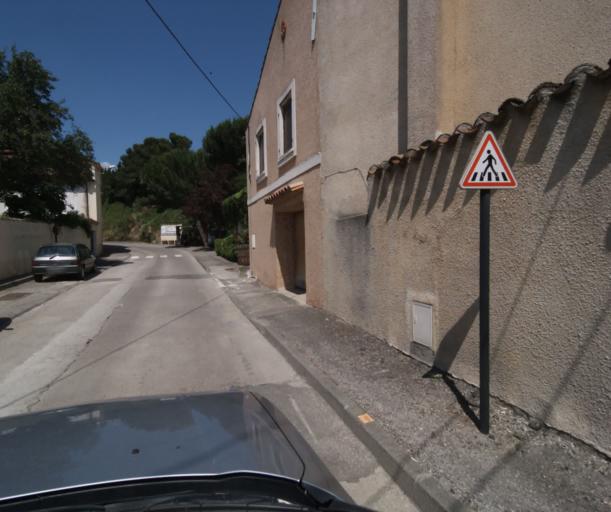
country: FR
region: Languedoc-Roussillon
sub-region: Departement de l'Aude
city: Limoux
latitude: 43.0521
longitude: 2.2227
